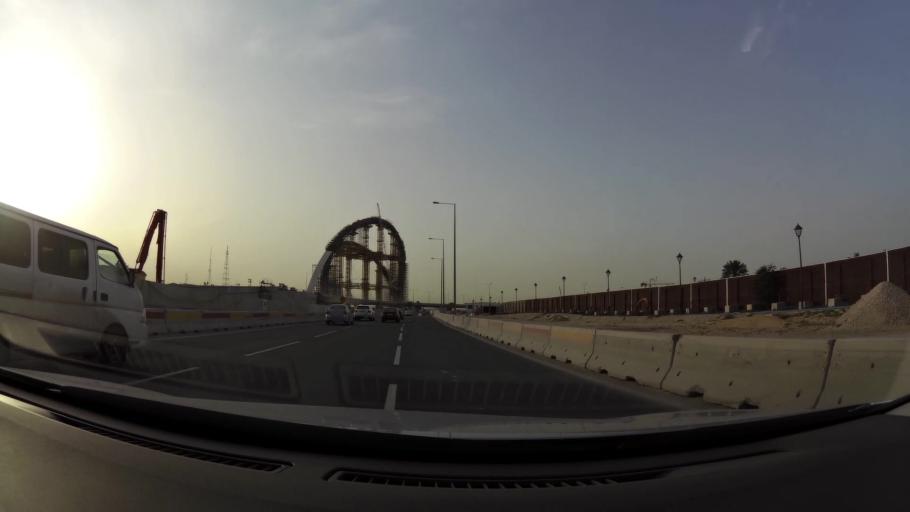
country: QA
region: Baladiyat ad Dawhah
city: Doha
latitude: 25.3325
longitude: 51.5212
